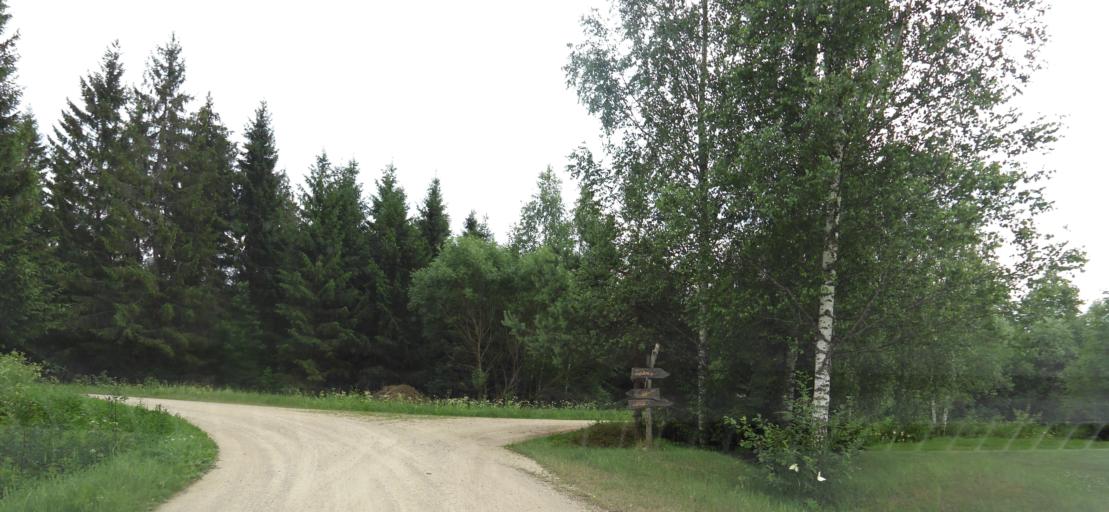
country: LV
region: Nereta
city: Nereta
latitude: 56.1949
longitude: 25.0742
